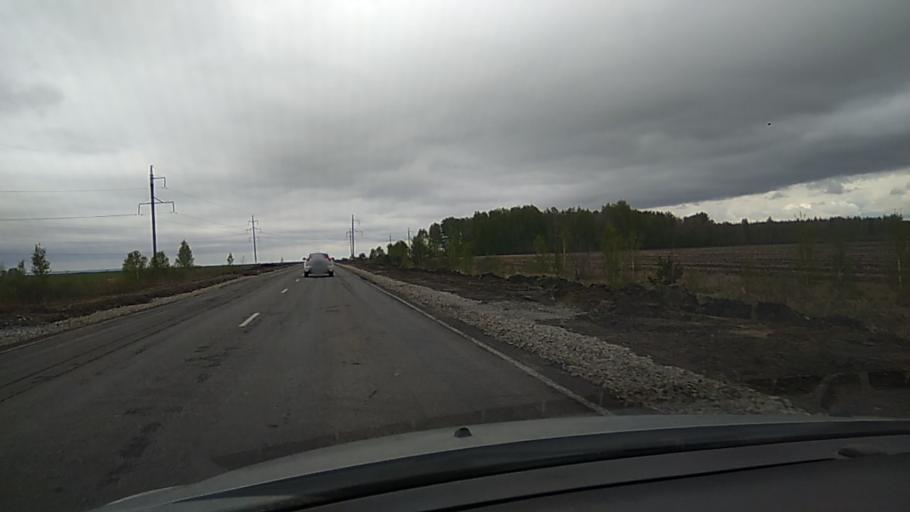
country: RU
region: Kurgan
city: Shadrinsk
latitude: 56.1452
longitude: 63.4888
